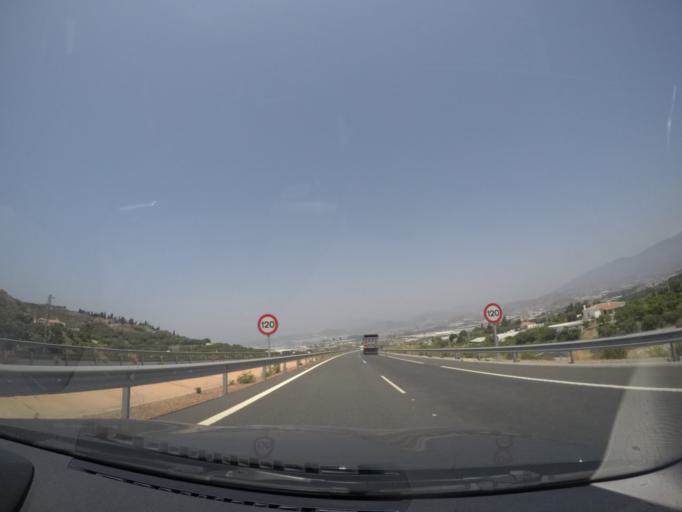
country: ES
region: Andalusia
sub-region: Provincia de Granada
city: El Varadero
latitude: 36.7183
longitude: -3.4608
